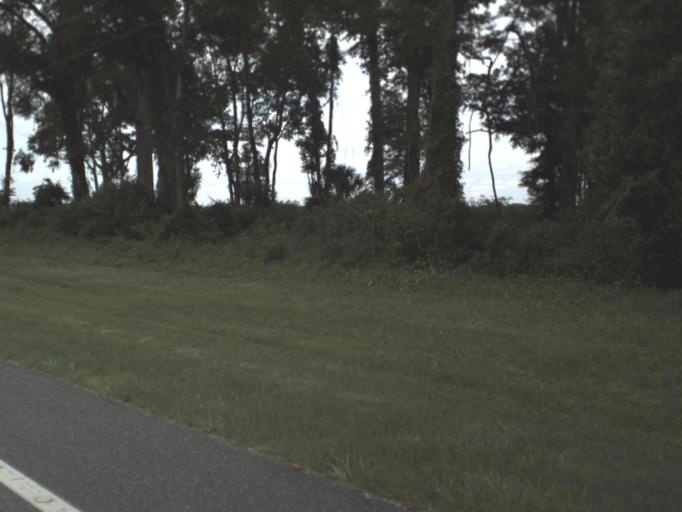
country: US
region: Florida
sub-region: Suwannee County
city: Wellborn
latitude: 30.0005
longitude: -82.8584
